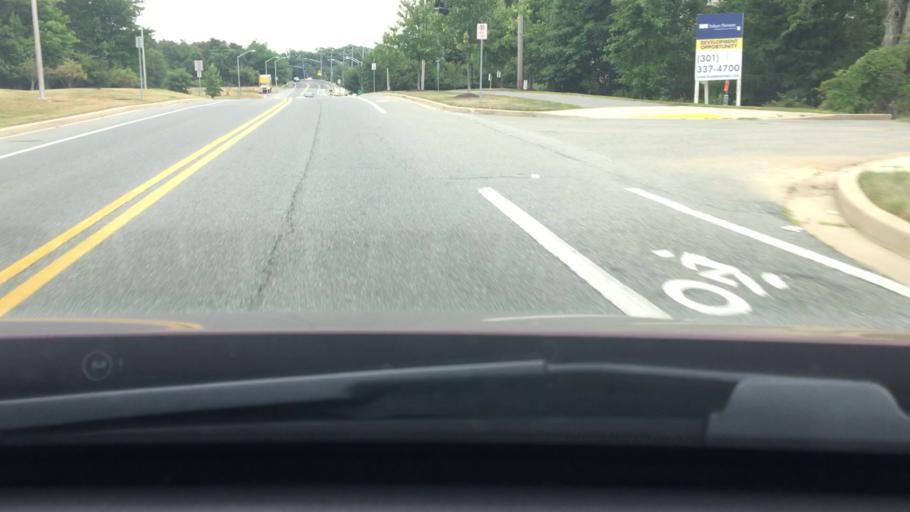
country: US
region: Maryland
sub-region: Prince George's County
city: Calverton
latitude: 39.0811
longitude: -76.9304
